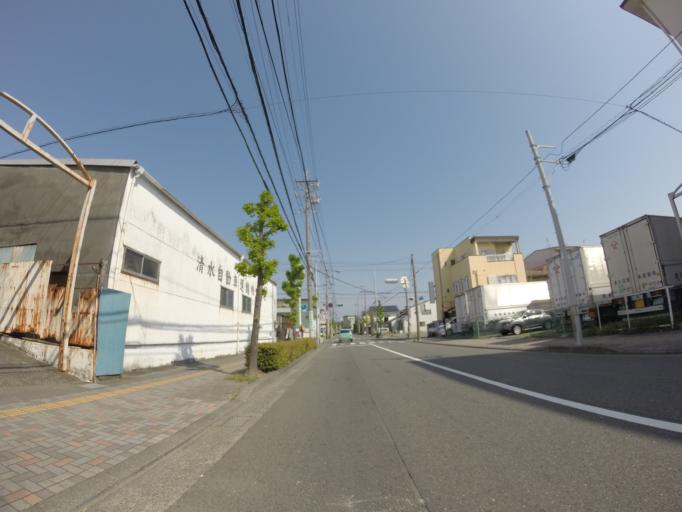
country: JP
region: Shizuoka
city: Shizuoka-shi
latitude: 35.0063
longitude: 138.4868
